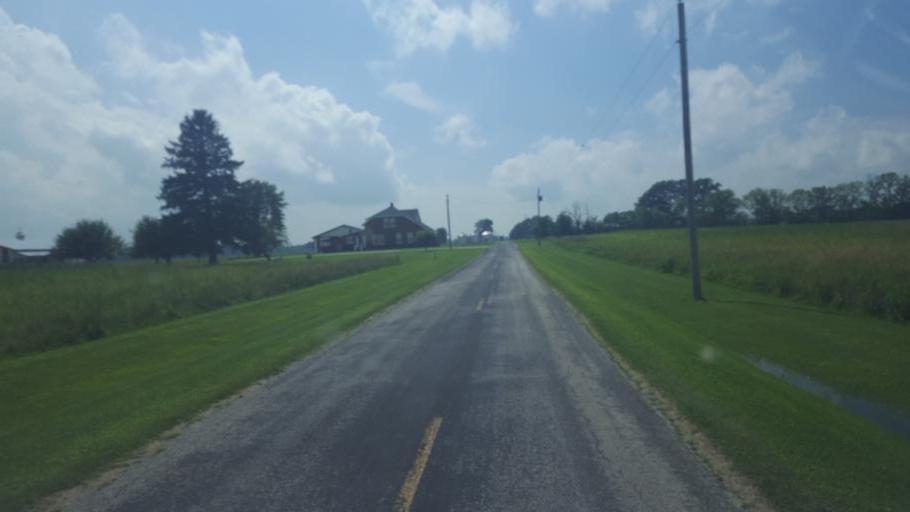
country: US
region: Ohio
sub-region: Union County
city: Richwood
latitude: 40.5665
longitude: -83.3562
